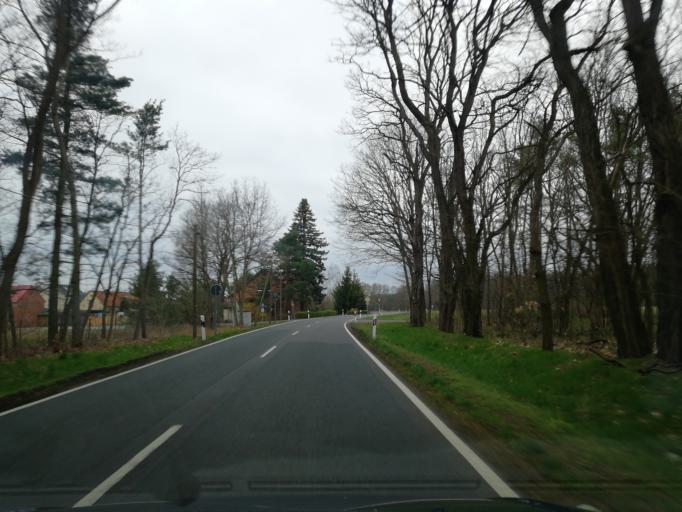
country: DE
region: Brandenburg
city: Vetschau
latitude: 51.7384
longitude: 14.0536
